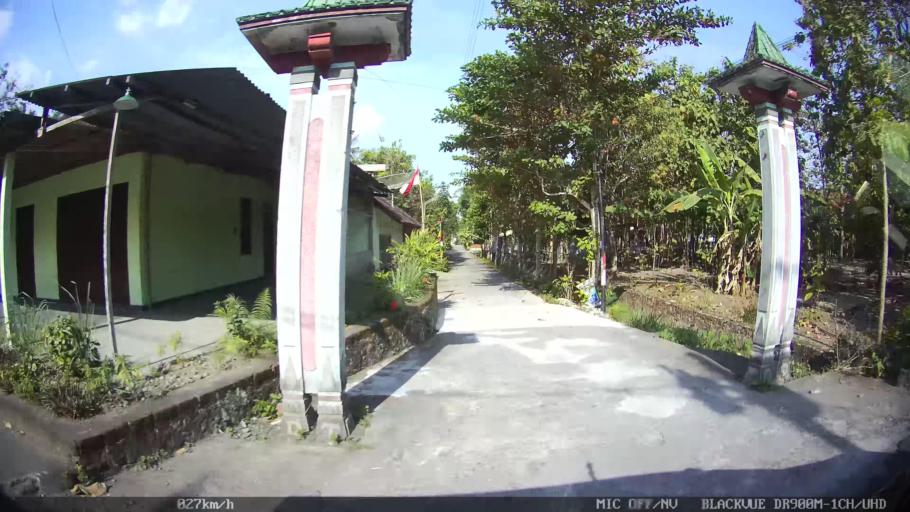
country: ID
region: Daerah Istimewa Yogyakarta
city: Kasihan
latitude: -7.8362
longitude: 110.3367
